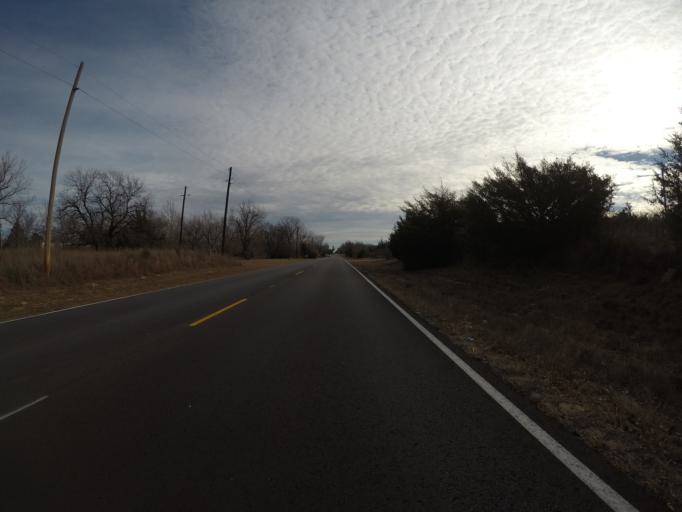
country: US
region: Kansas
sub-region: Reno County
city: Hutchinson
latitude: 38.1156
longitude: -97.8728
